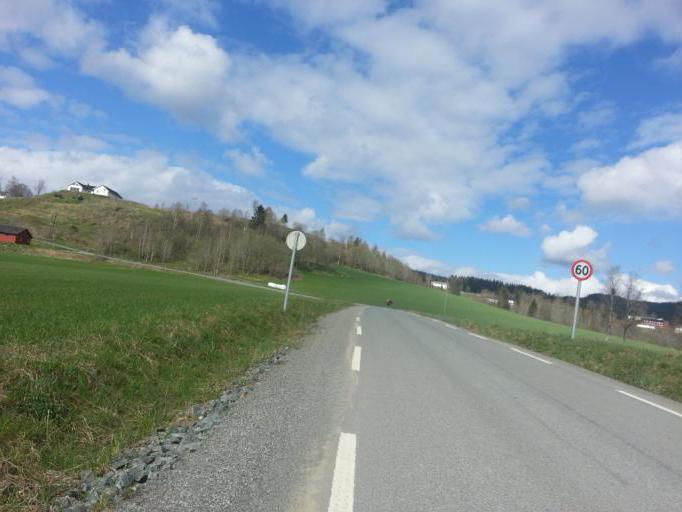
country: NO
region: Nord-Trondelag
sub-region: Levanger
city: Skogn
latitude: 63.6331
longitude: 11.2769
